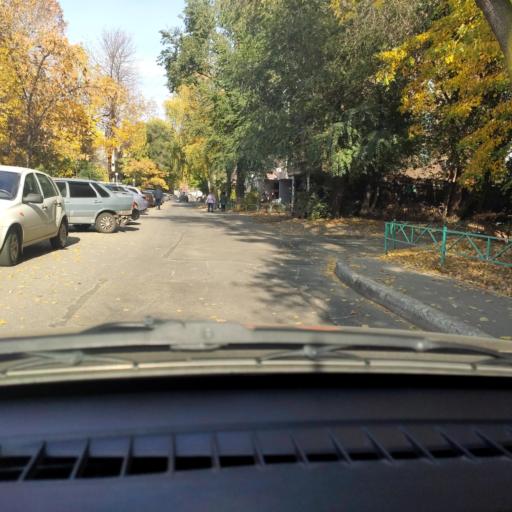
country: RU
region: Samara
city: Tol'yatti
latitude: 53.5243
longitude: 49.2733
